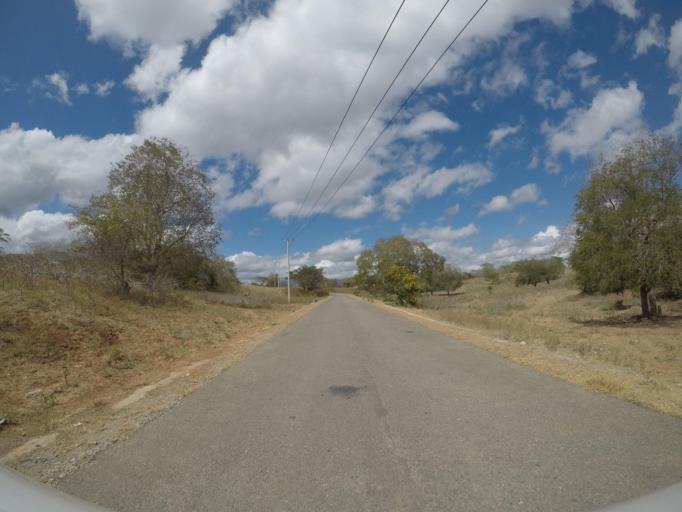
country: TL
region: Lautem
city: Lospalos
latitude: -8.4291
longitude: 126.8307
